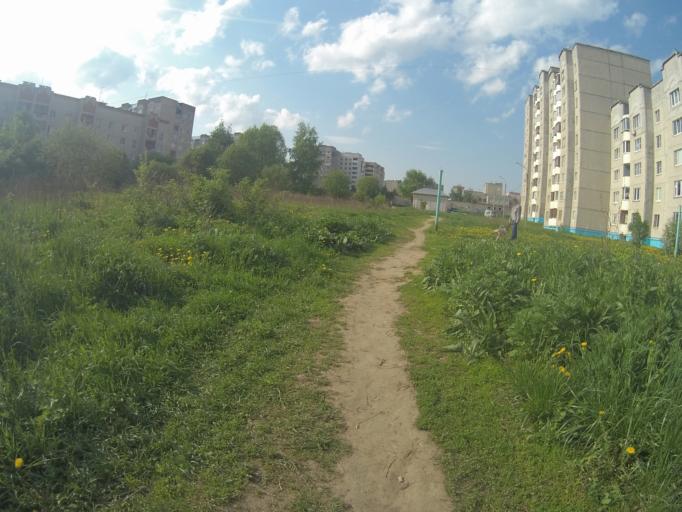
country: RU
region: Vladimir
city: Kommunar
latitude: 56.1665
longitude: 40.4495
